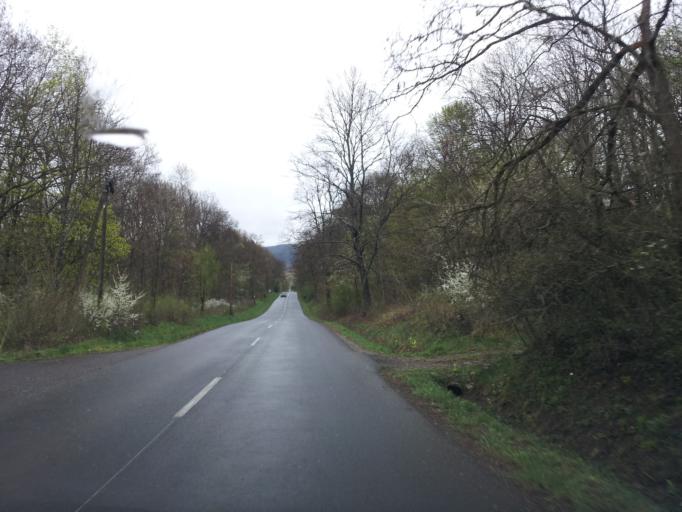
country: HU
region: Borsod-Abauj-Zemplen
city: Putnok
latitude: 48.4560
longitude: 20.4845
